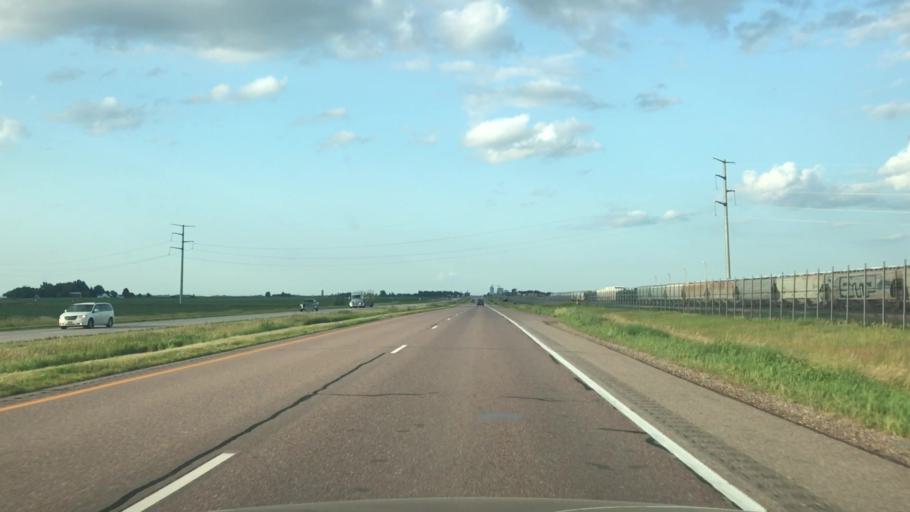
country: US
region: Minnesota
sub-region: Nobles County
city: Worthington
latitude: 43.6697
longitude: -95.5160
